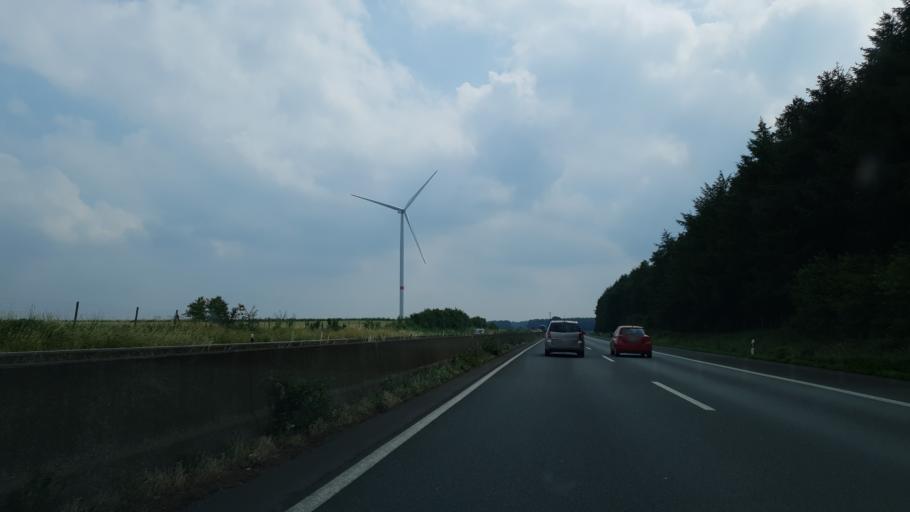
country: DE
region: North Rhine-Westphalia
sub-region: Regierungsbezirk Munster
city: Velen
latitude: 51.8390
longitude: 7.0045
